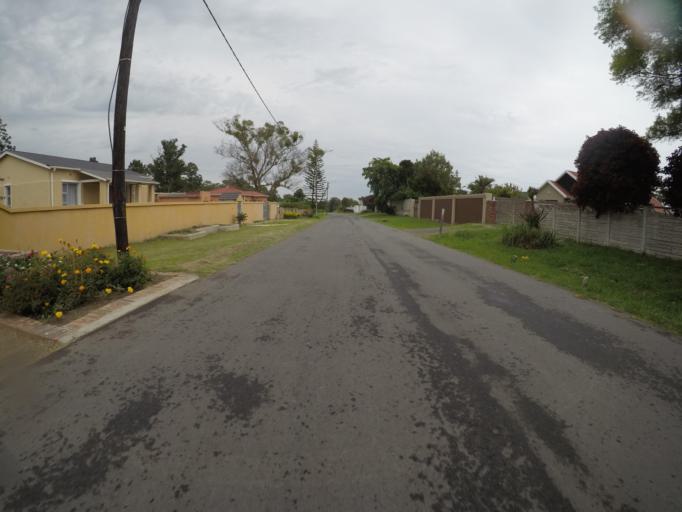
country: ZA
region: Eastern Cape
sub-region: Buffalo City Metropolitan Municipality
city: East London
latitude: -32.9659
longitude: 27.8320
